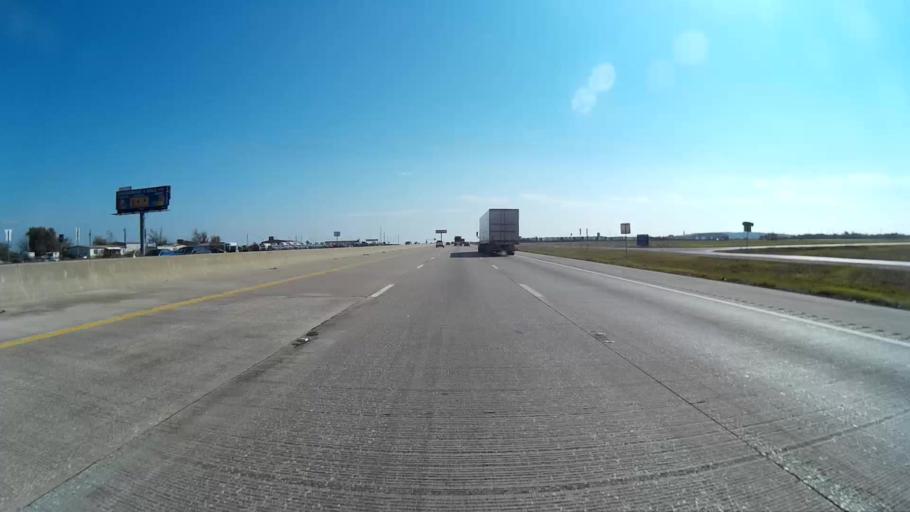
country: US
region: Texas
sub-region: Dallas County
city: Wilmer
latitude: 32.5781
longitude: -96.6730
